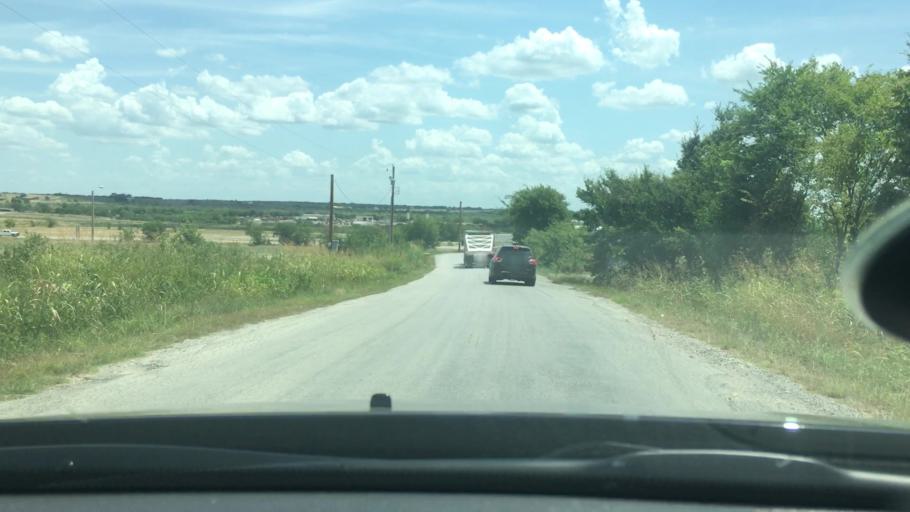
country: US
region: Oklahoma
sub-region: Carter County
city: Ardmore
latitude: 34.0783
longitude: -97.1533
